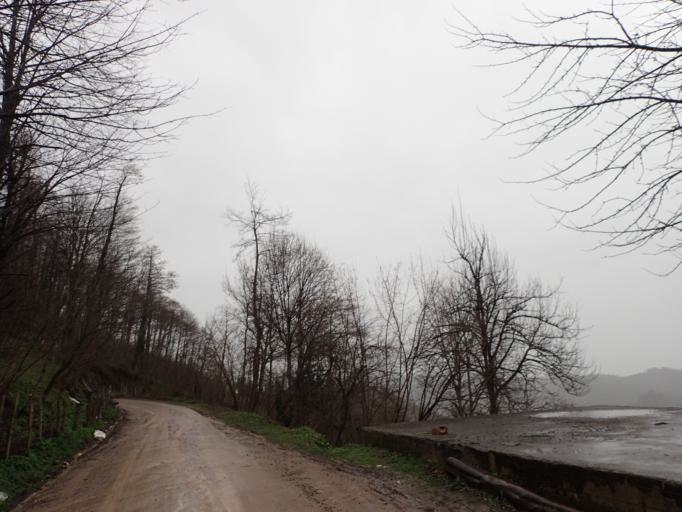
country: TR
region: Ordu
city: Camas
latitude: 40.8812
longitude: 37.4993
